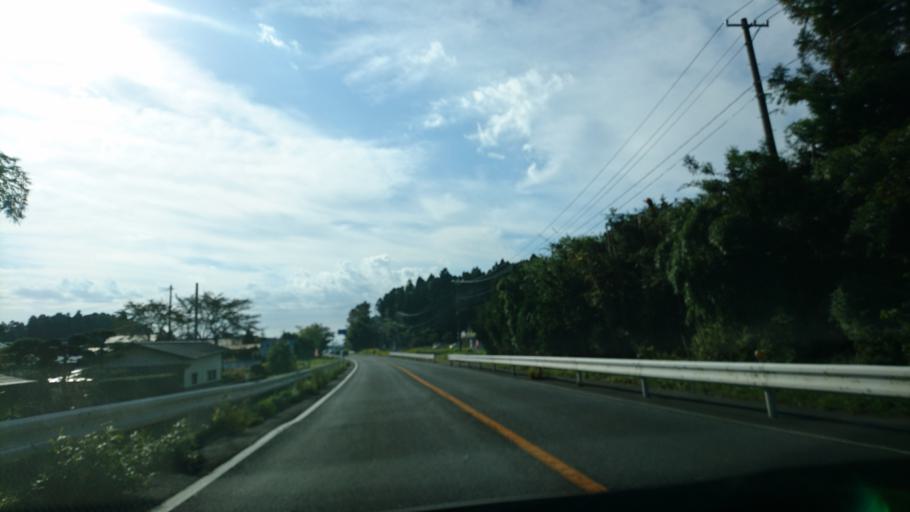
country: JP
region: Miyagi
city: Furukawa
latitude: 38.6257
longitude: 140.9825
